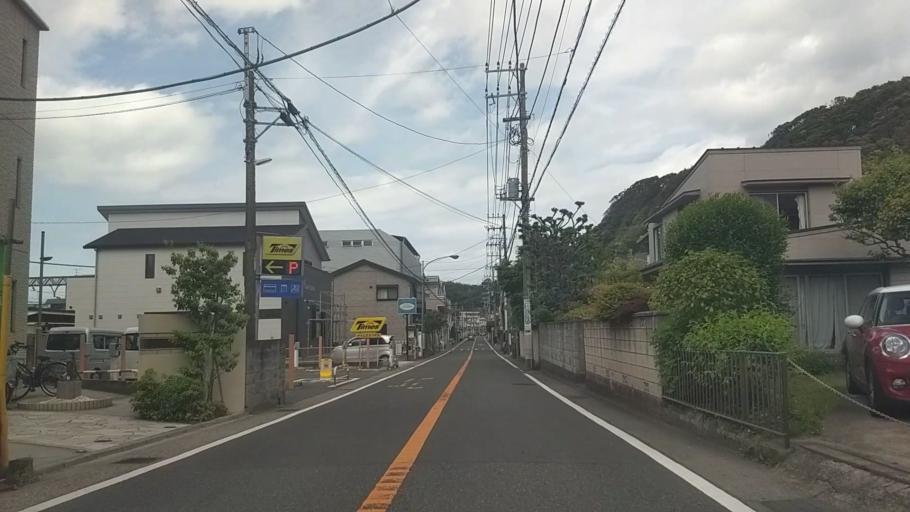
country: JP
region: Kanagawa
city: Zushi
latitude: 35.2978
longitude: 139.5783
